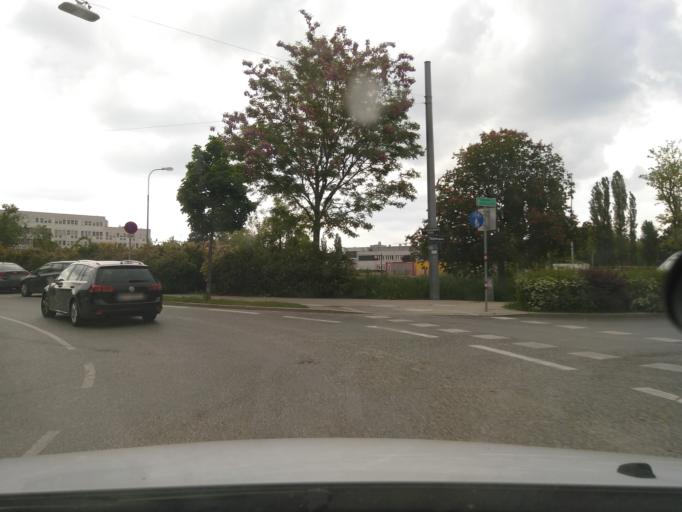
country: AT
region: Lower Austria
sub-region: Politischer Bezirk Modling
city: Perchtoldsdorf
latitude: 48.1512
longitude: 16.2961
